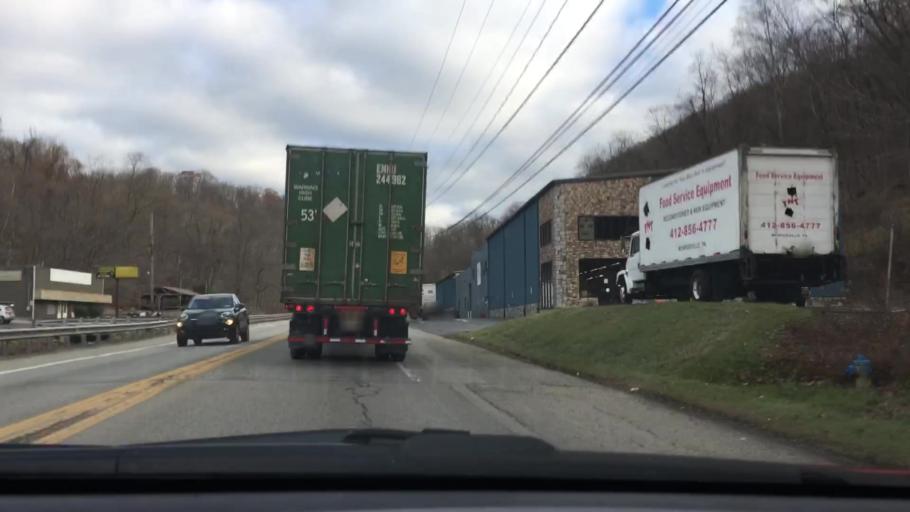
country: US
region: Pennsylvania
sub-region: Allegheny County
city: Pitcairn
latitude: 40.3991
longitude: -79.7677
